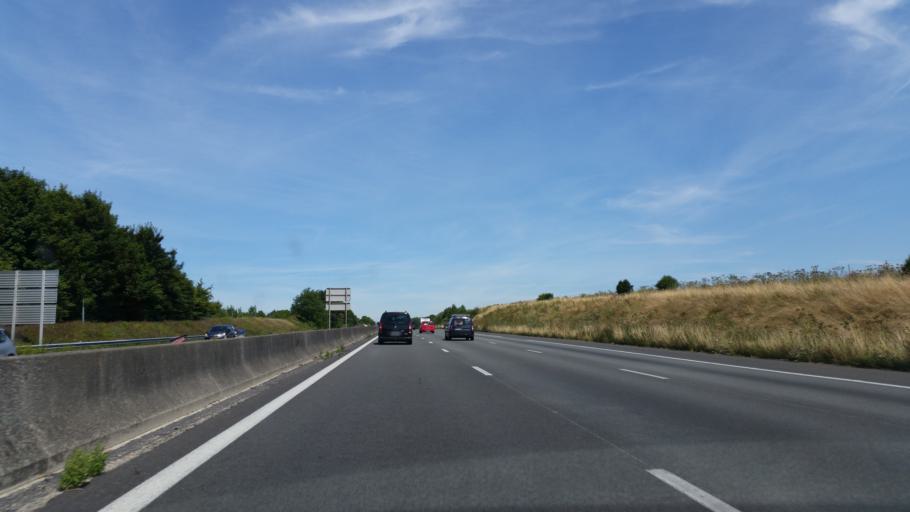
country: FR
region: Picardie
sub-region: Departement de la Somme
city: Peronne
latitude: 49.9811
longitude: 2.8679
